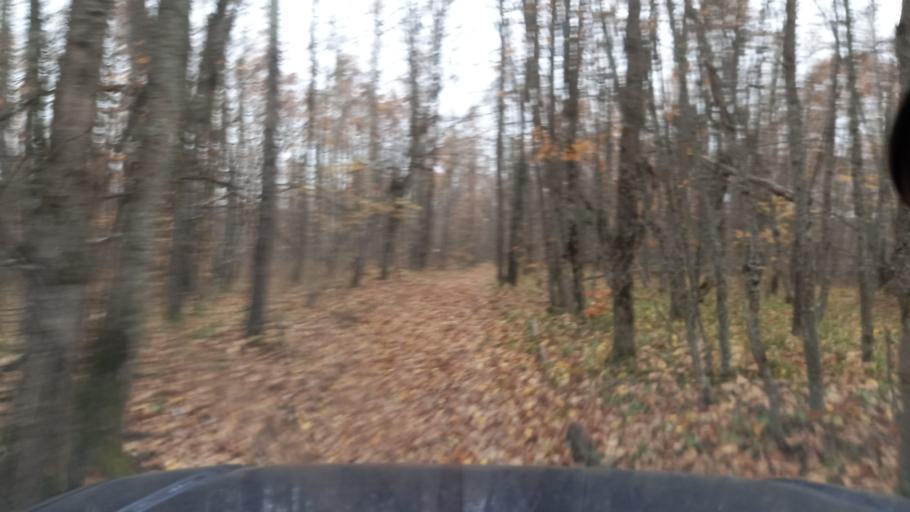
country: RU
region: Krasnodarskiy
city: Goryachiy Klyuch
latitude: 44.4981
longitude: 39.2767
